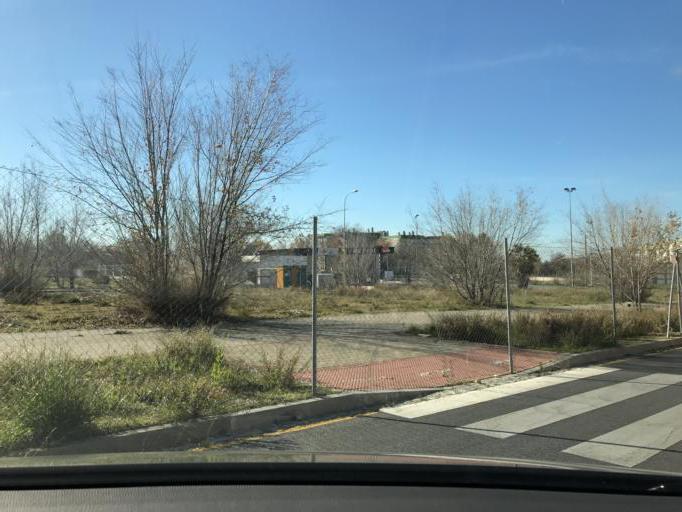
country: ES
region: Andalusia
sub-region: Provincia de Granada
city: Pulianas
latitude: 37.2114
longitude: -3.6087
